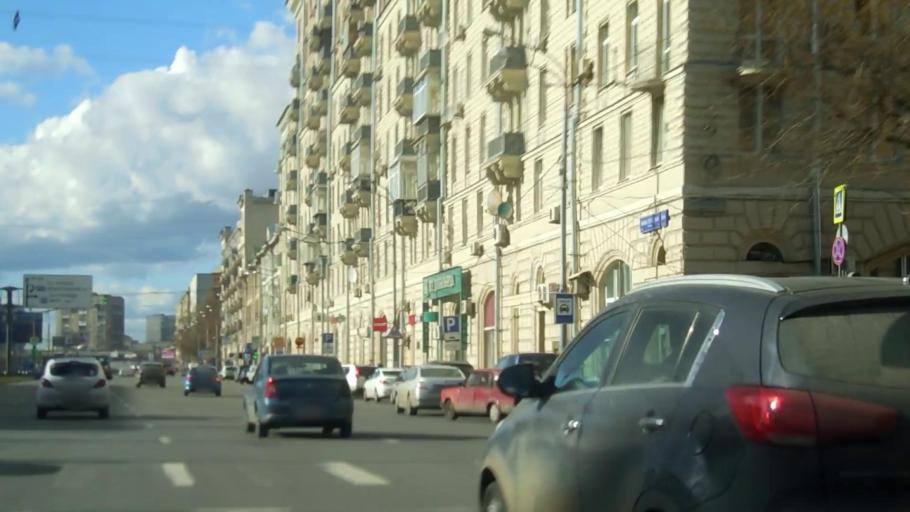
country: RU
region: Moscow
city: Mar'ina Roshcha
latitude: 55.7860
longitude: 37.5946
